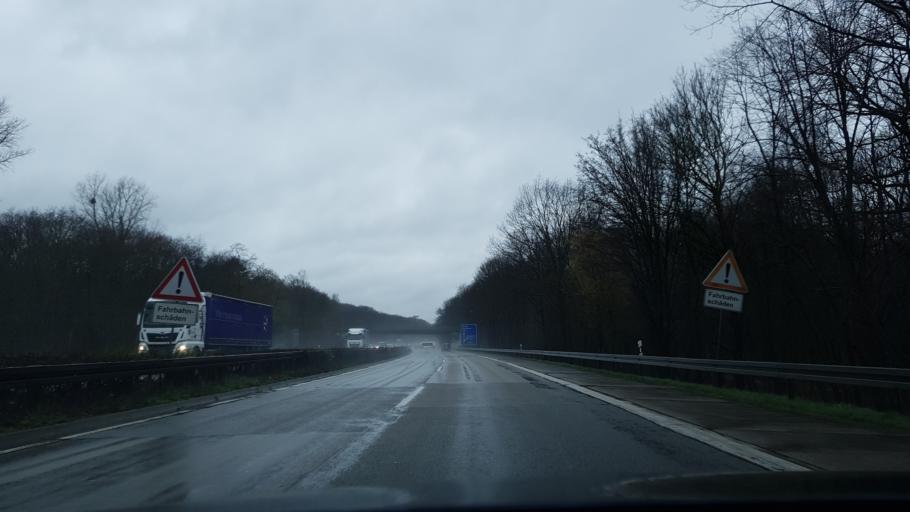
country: DE
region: North Rhine-Westphalia
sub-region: Regierungsbezirk Dusseldorf
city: Erkrath
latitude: 51.1802
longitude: 6.8815
